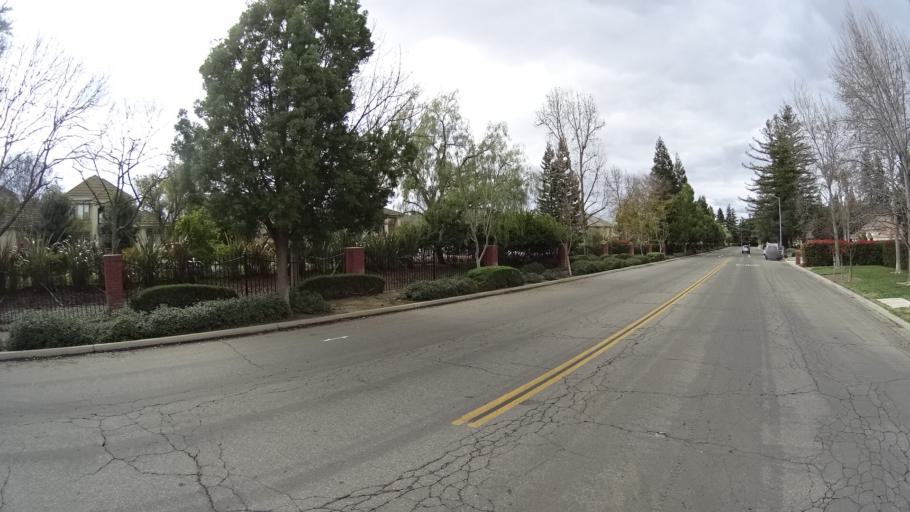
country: US
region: California
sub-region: Fresno County
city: Fresno
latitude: 36.8444
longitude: -119.8449
